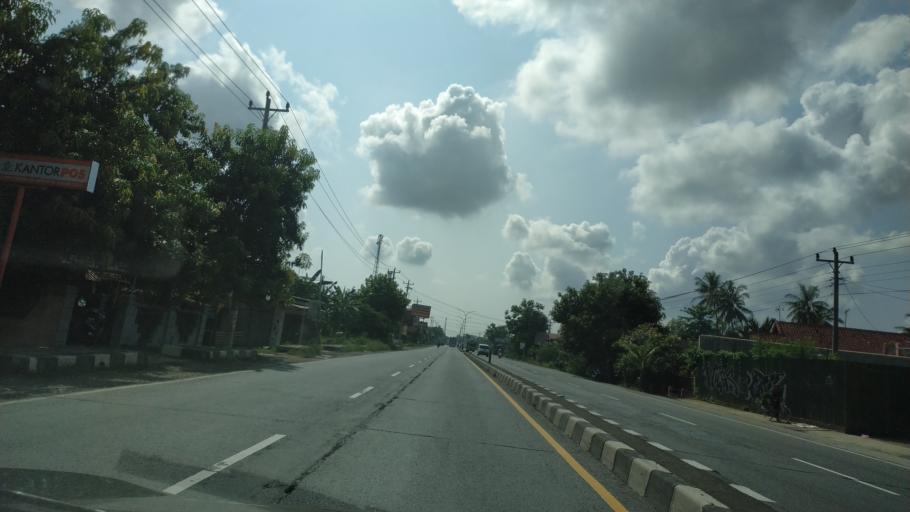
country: ID
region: Central Java
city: Comal
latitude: -6.8864
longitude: 109.5523
